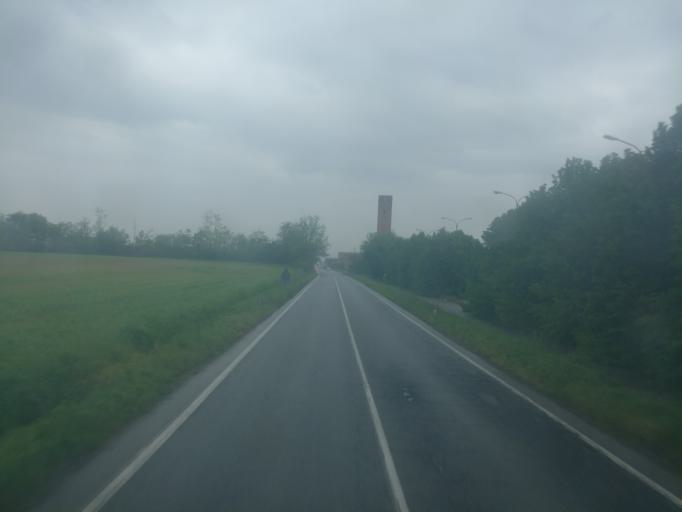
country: IT
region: Piedmont
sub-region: Provincia di Torino
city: Carignano
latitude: 44.8867
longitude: 7.6680
